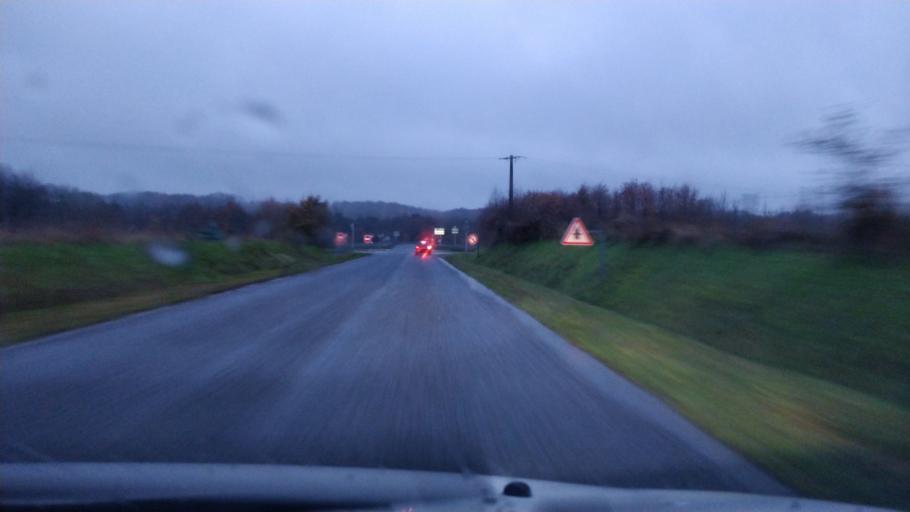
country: FR
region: Brittany
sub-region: Departement du Morbihan
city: Meneac
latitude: 48.1927
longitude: -2.5163
